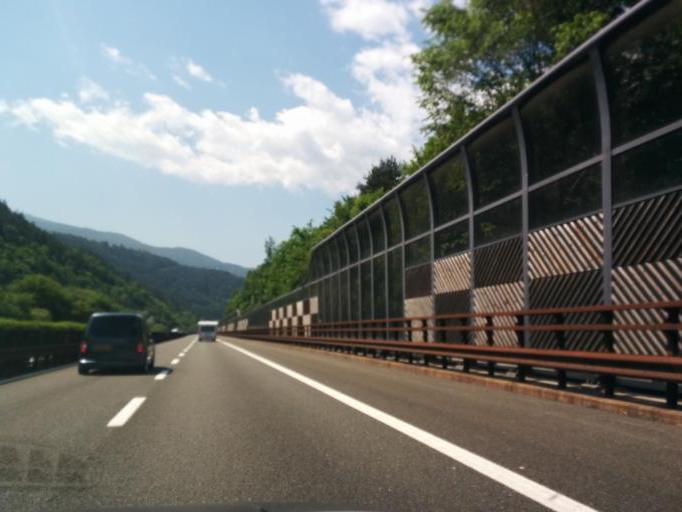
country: IT
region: Trentino-Alto Adige
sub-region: Bolzano
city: Velturno
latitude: 46.6679
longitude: 11.6149
